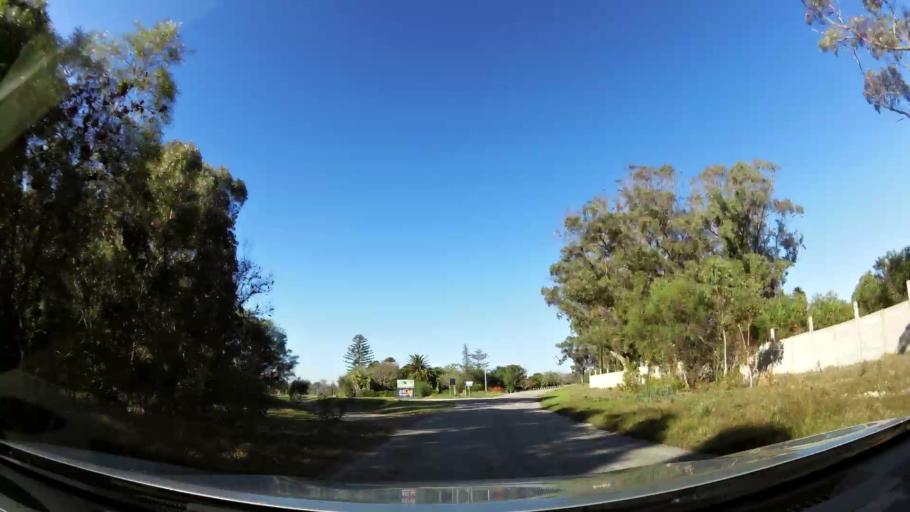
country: ZA
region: Eastern Cape
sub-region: Nelson Mandela Bay Metropolitan Municipality
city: Port Elizabeth
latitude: -33.9860
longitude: 25.6333
